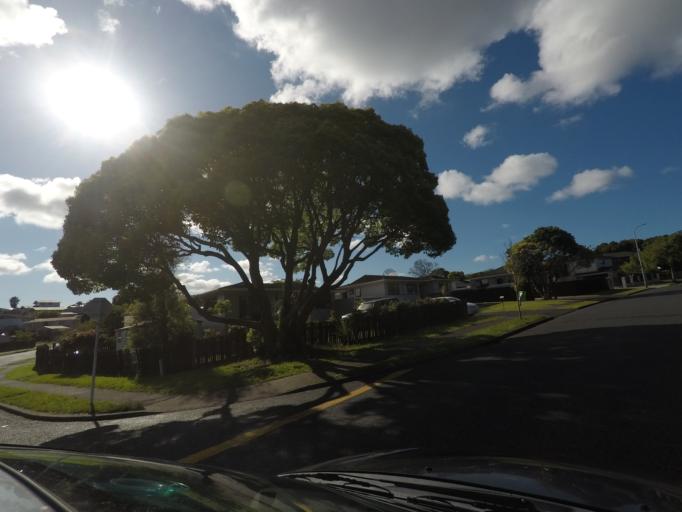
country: NZ
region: Auckland
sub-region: Auckland
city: Manukau City
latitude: -36.9865
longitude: 174.8897
